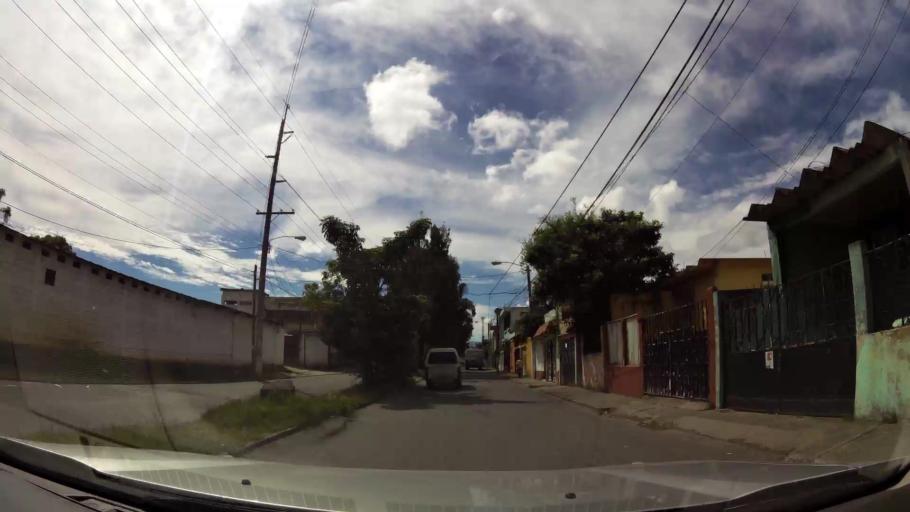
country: GT
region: Guatemala
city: Mixco
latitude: 14.6651
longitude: -90.5690
